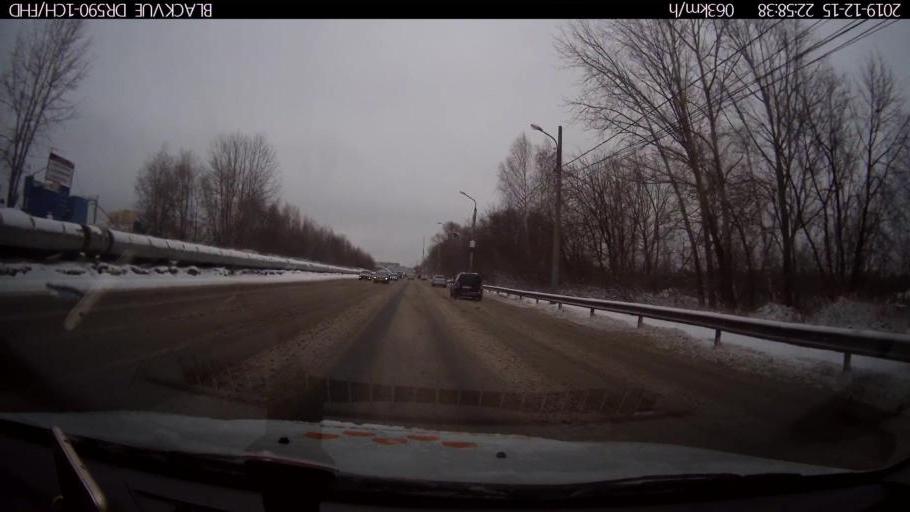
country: RU
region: Nizjnij Novgorod
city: Nizhniy Novgorod
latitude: 56.3430
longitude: 43.8992
